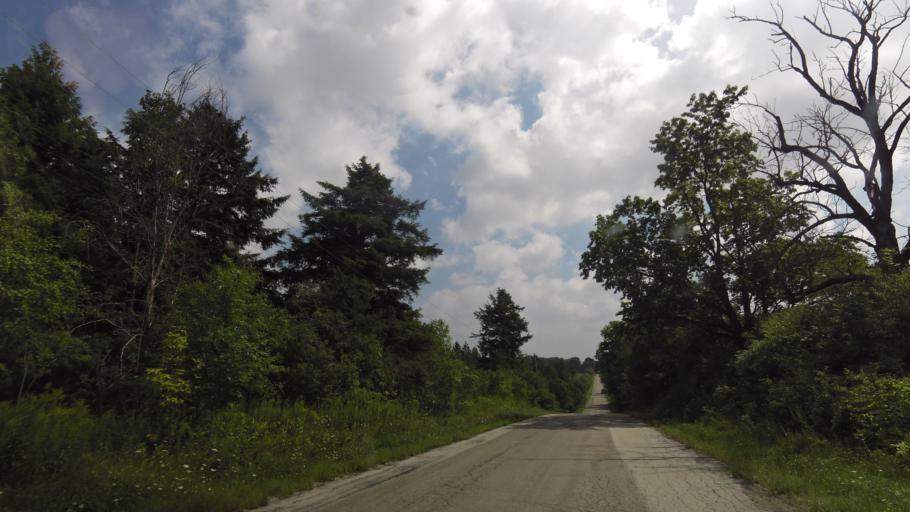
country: CA
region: Ontario
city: Oshawa
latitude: 44.0000
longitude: -78.8761
